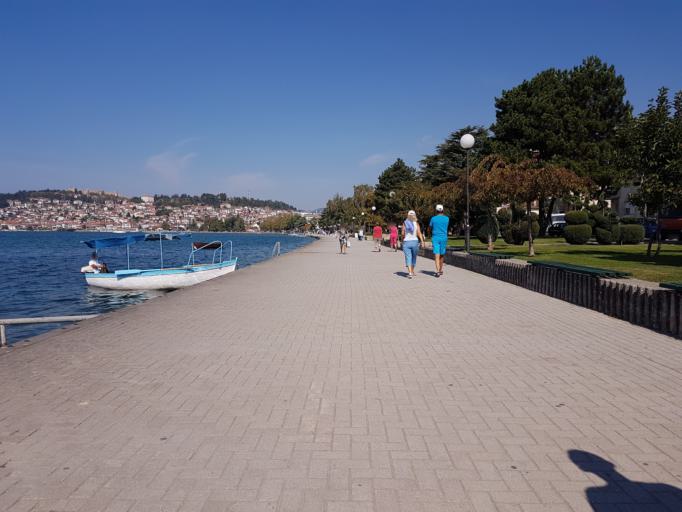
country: MK
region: Ohrid
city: Ohrid
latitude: 41.1070
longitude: 20.8069
